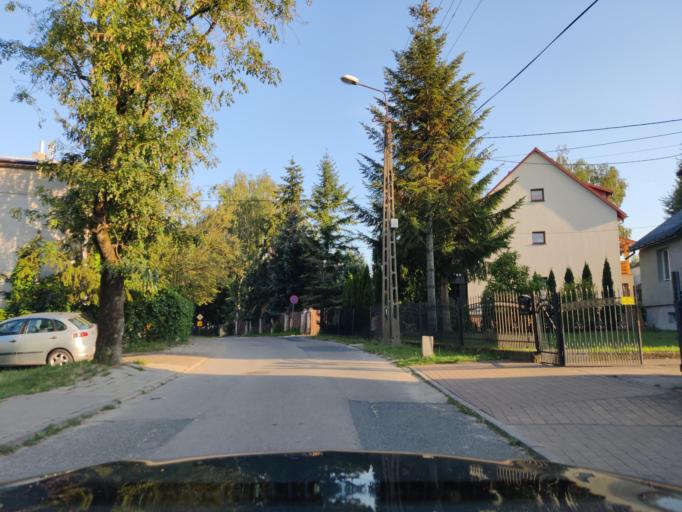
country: PL
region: Masovian Voivodeship
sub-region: Powiat pultuski
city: Pultusk
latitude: 52.7069
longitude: 21.0834
